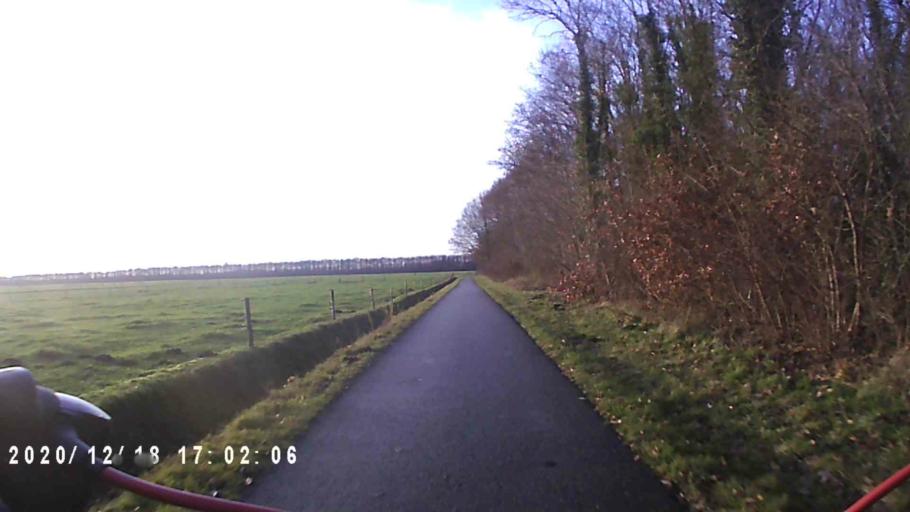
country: NL
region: Drenthe
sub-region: Gemeente Tynaarlo
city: Tynaarlo
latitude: 53.0631
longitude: 6.6373
